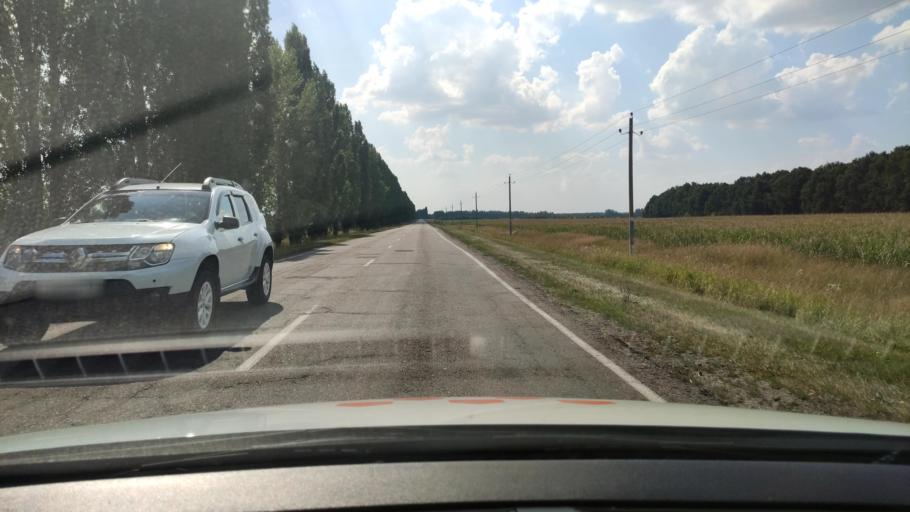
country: RU
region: Voronezj
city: Sadovoye
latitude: 51.7617
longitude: 40.4553
